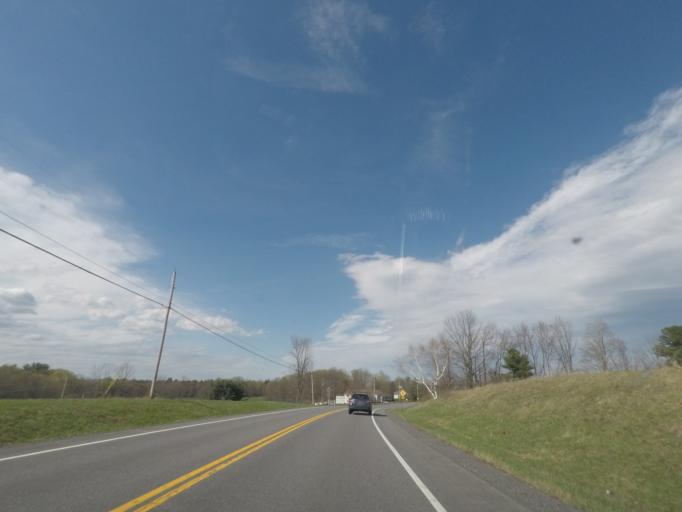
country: US
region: New York
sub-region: Greene County
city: Cairo
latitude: 42.4613
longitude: -74.0048
